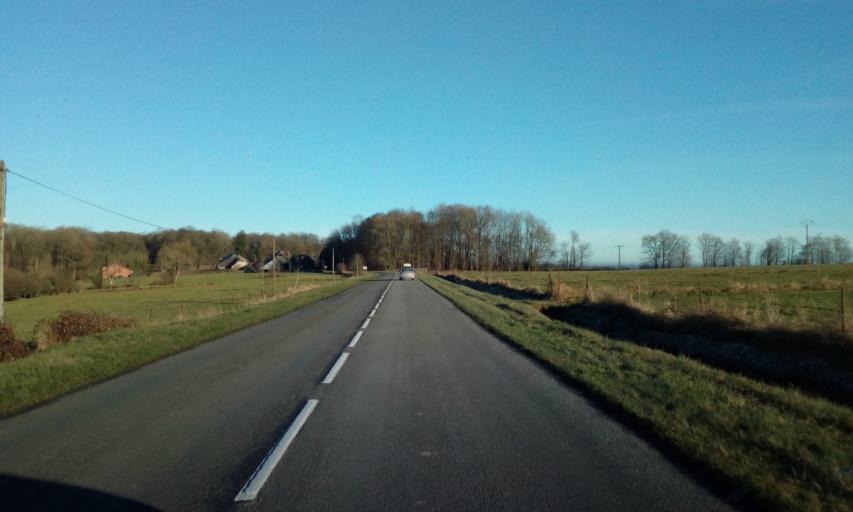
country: FR
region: Picardie
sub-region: Departement de l'Aisne
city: Rozoy-sur-Serre
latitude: 49.7205
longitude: 4.2635
